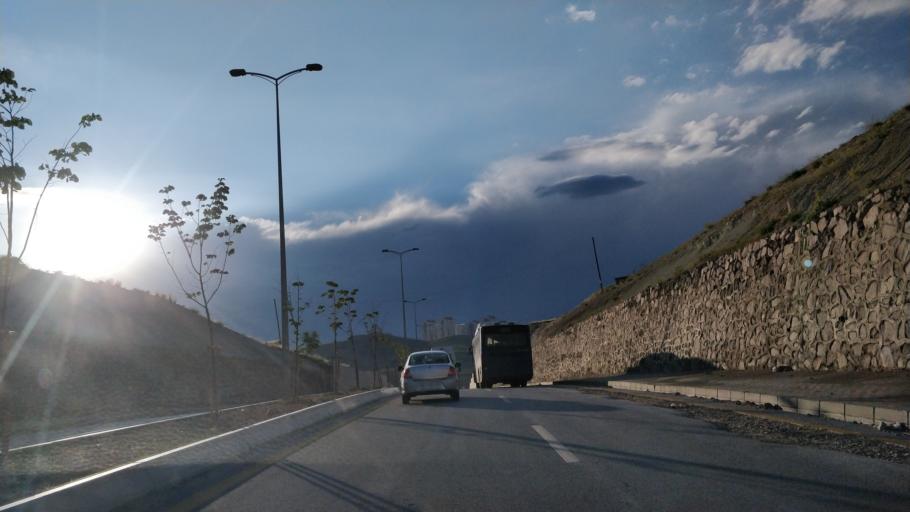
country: TR
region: Ankara
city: Etimesgut
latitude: 39.8321
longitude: 32.5547
